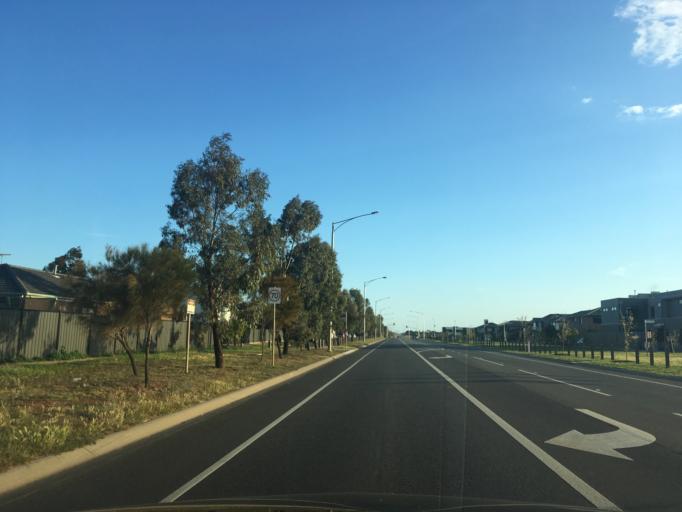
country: AU
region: Victoria
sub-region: Wyndham
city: Hoppers Crossing
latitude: -37.8894
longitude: 144.7180
